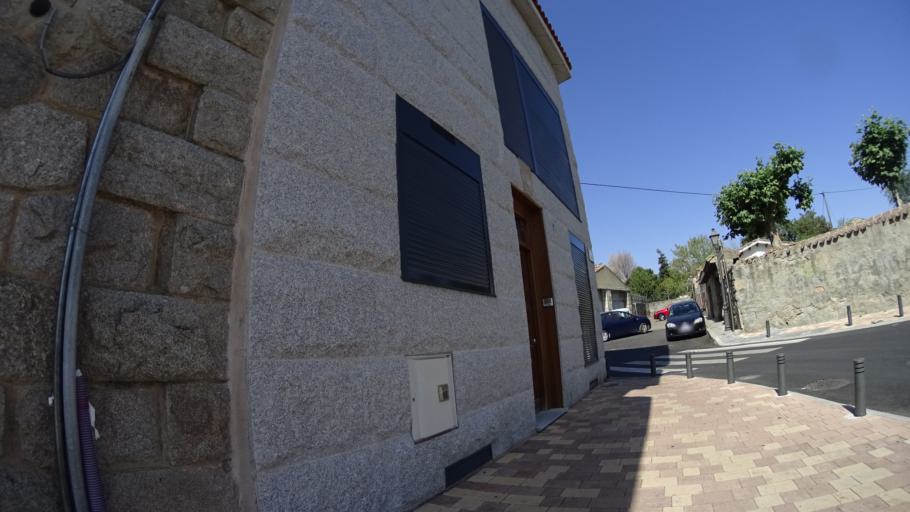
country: ES
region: Madrid
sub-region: Provincia de Madrid
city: Guadarrama
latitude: 40.6749
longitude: -4.0905
